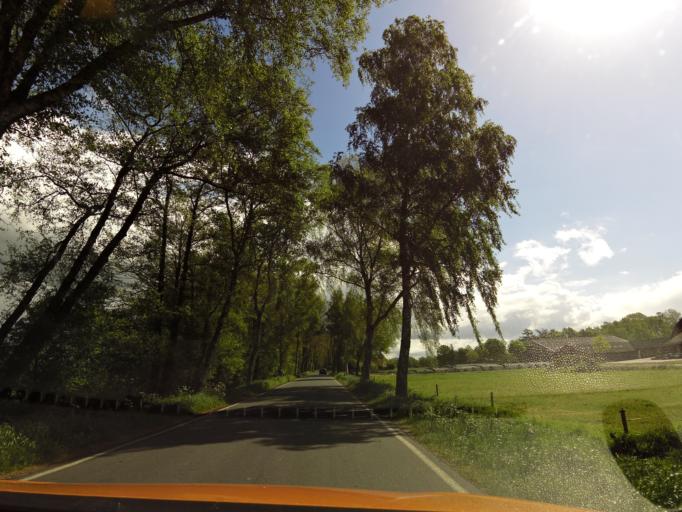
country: DE
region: Lower Saxony
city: Hude
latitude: 53.1587
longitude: 8.3942
